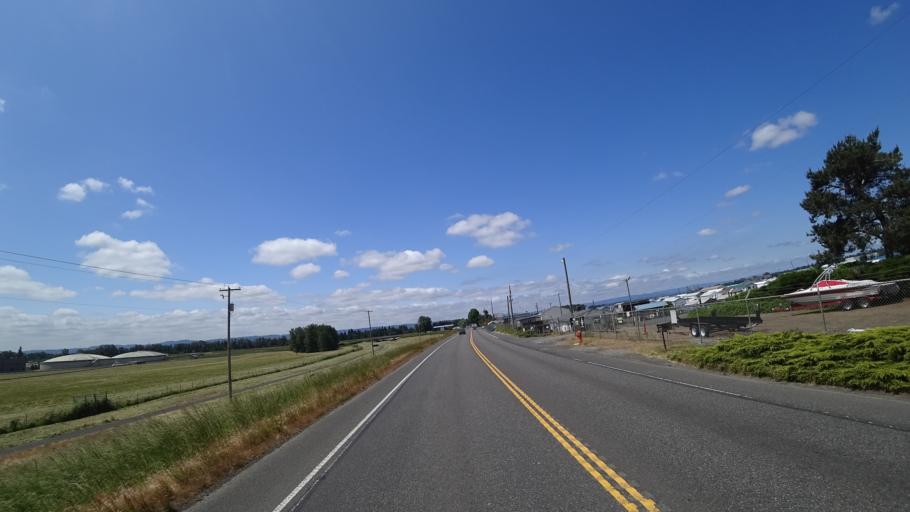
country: US
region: Washington
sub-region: Clark County
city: Vancouver
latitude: 45.6003
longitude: -122.6303
